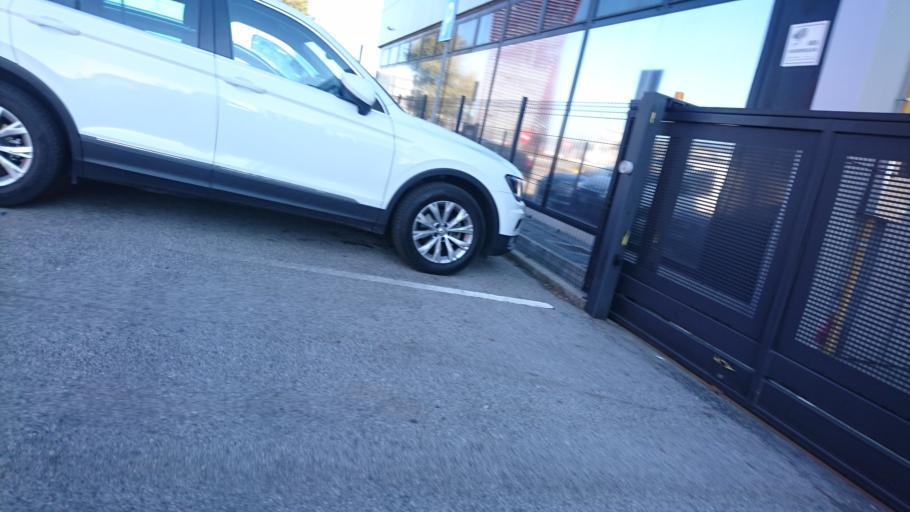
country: IT
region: Veneto
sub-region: Provincia di Padova
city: Cadoneghe
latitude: 45.4140
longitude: 11.9203
